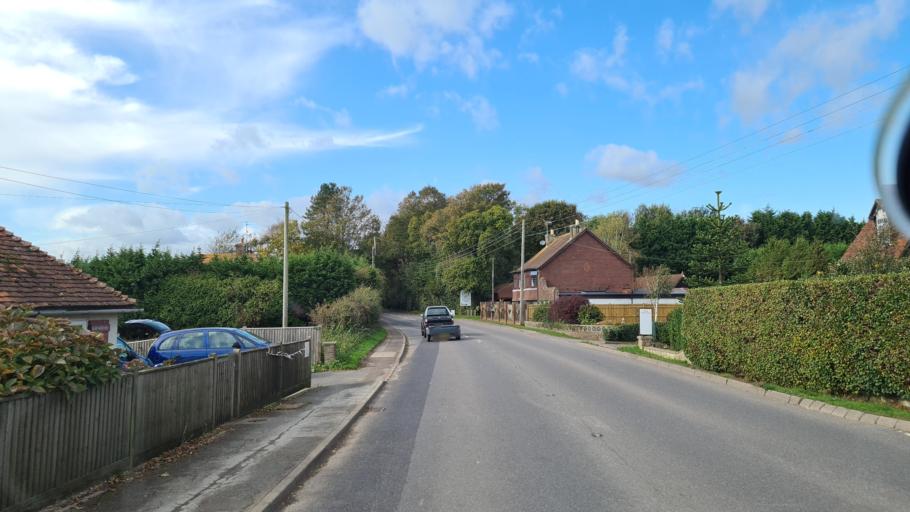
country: GB
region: England
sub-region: East Sussex
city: Bodle Street
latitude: 50.8863
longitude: 0.3374
